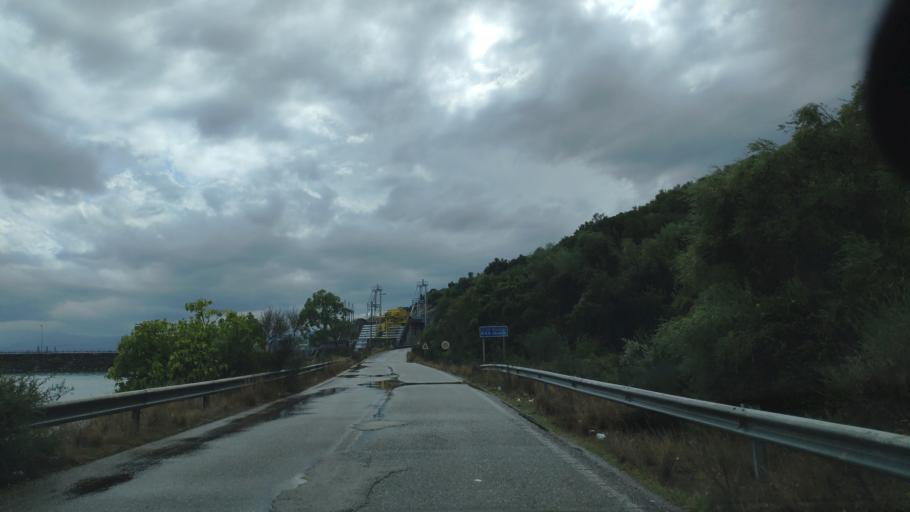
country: GR
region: West Greece
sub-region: Nomos Aitolias kai Akarnanias
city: Neapolis
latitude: 38.6794
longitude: 21.3241
